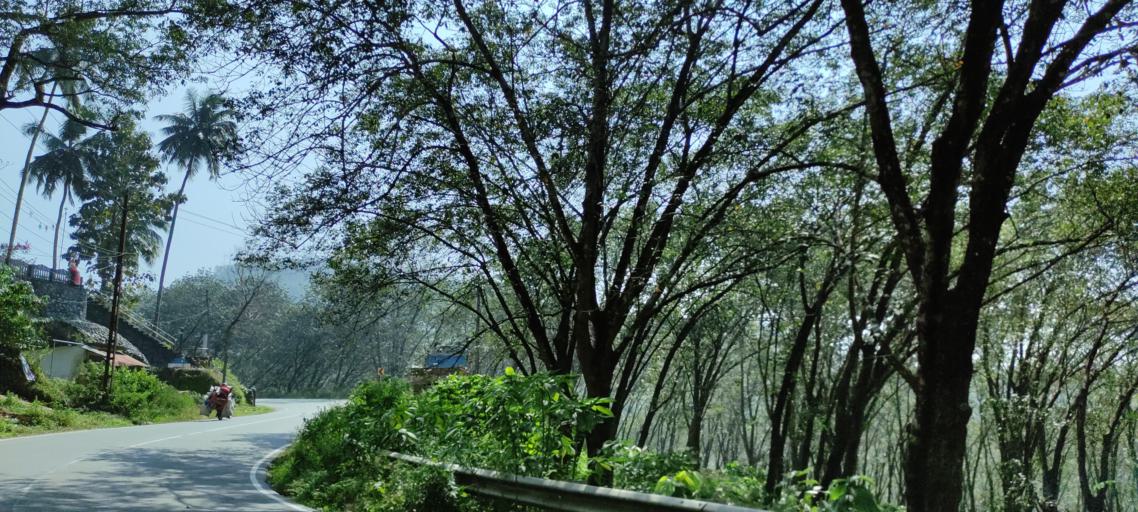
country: IN
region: Kerala
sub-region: Kollam
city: Punalur
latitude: 8.9725
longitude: 77.0660
